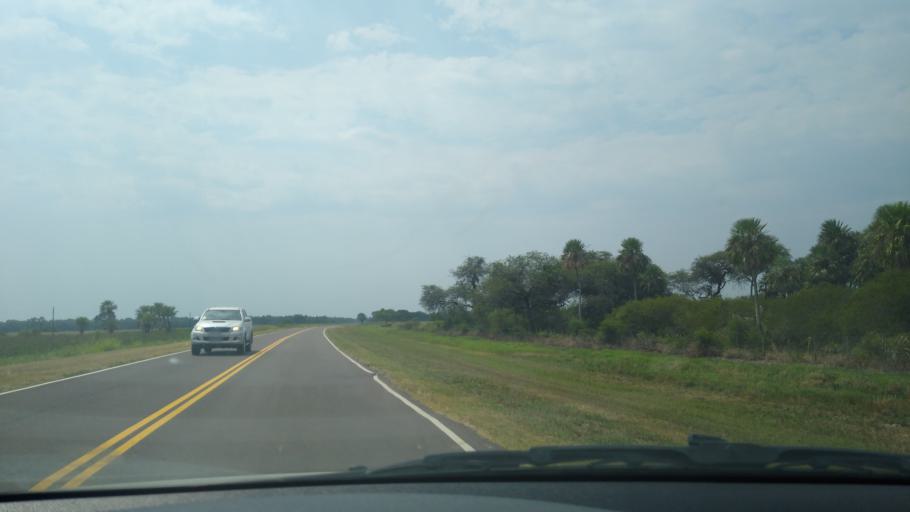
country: AR
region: Chaco
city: Margarita Belen
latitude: -27.0693
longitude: -58.9631
